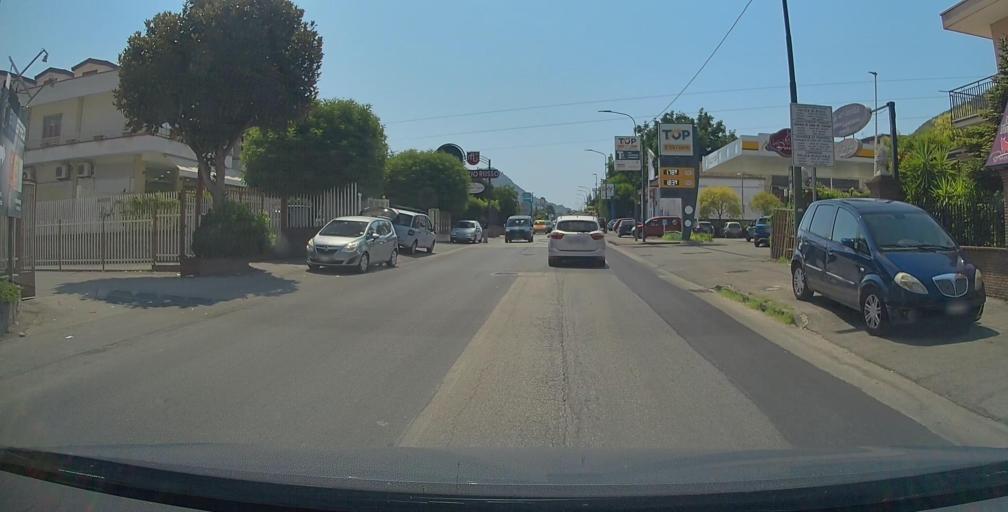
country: IT
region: Campania
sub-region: Provincia di Salerno
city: Nocera Superiore
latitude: 40.7274
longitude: 14.6912
